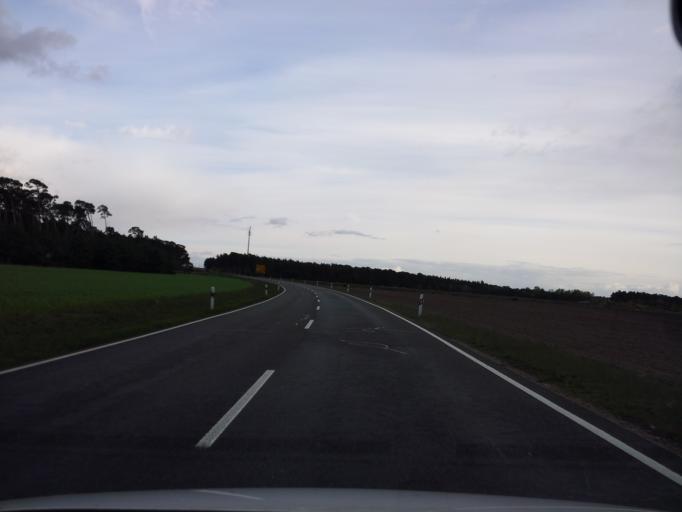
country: DE
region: Brandenburg
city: Heinersbruck
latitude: 51.8341
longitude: 14.5154
